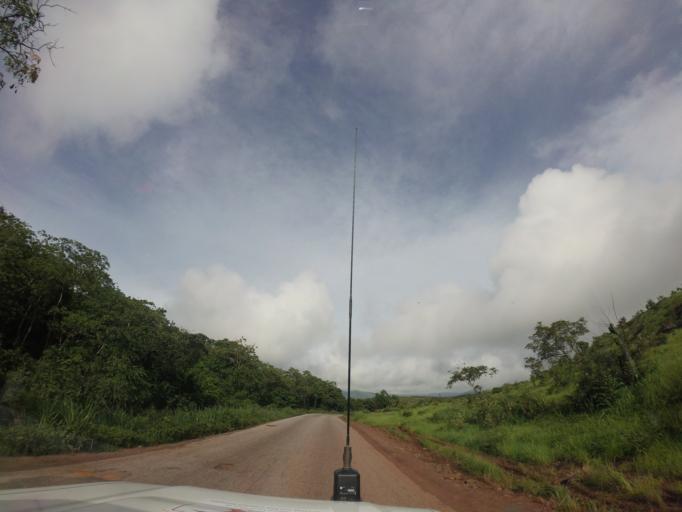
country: GN
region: Kindia
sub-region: Coyah
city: Coyah
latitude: 9.8408
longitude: -13.1456
